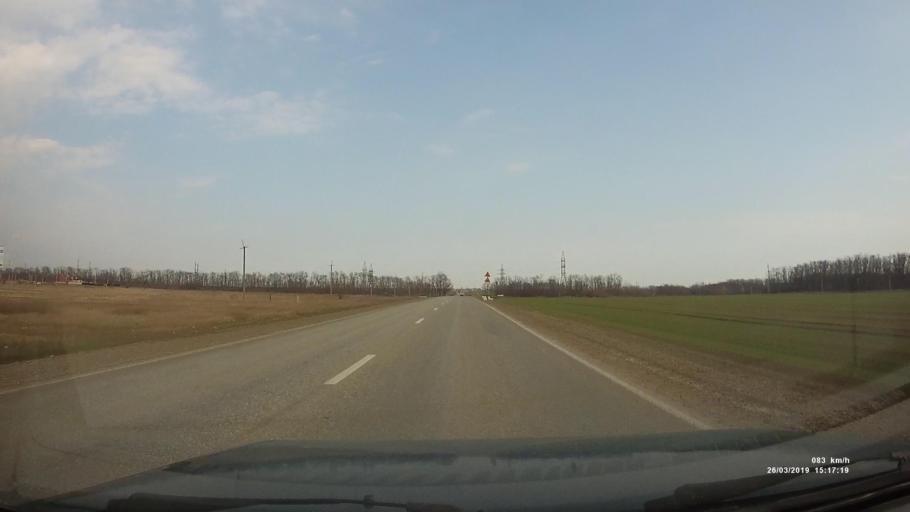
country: RU
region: Rostov
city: Taganrog
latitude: 47.2866
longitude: 38.9180
